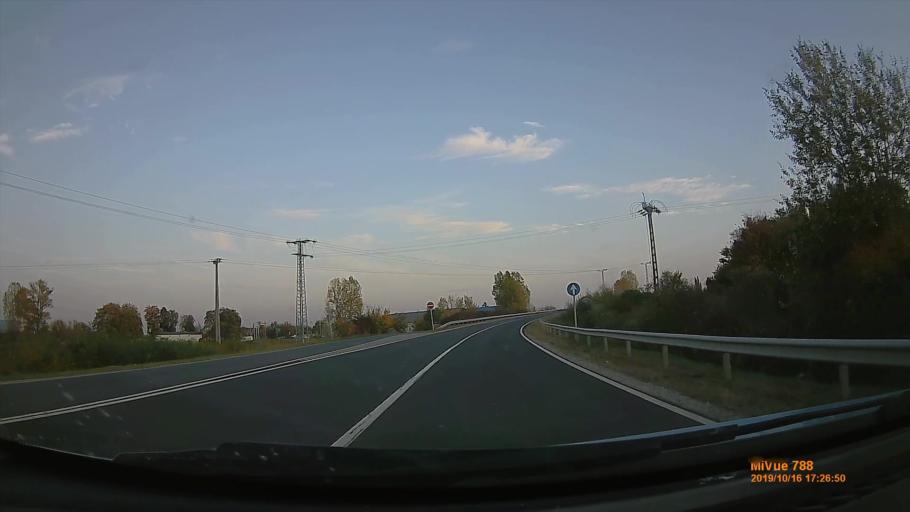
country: HU
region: Heves
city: Fuzesabony
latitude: 47.7405
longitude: 20.4064
